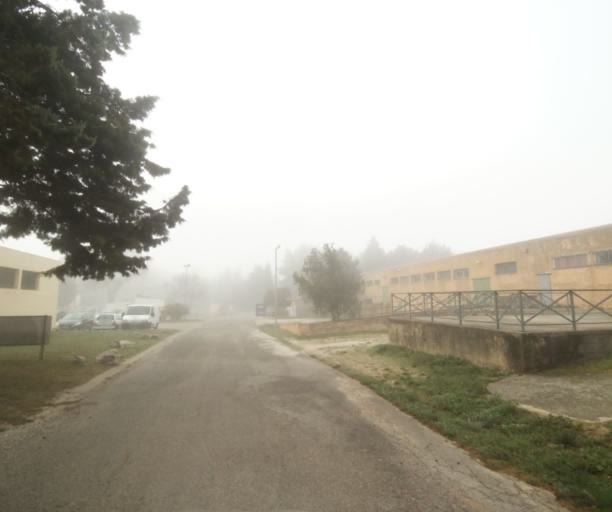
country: FR
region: Provence-Alpes-Cote d'Azur
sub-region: Departement des Bouches-du-Rhone
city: Eguilles
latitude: 43.5443
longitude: 5.3658
